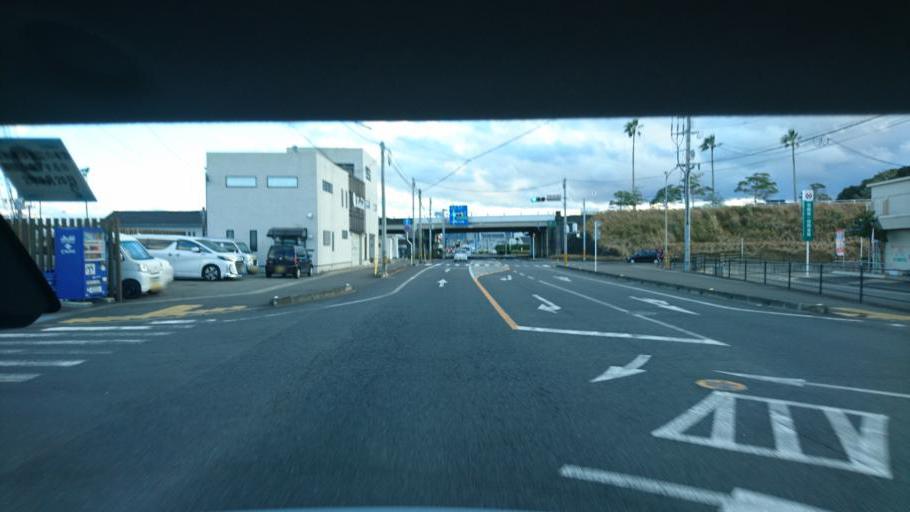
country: JP
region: Miyazaki
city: Miyazaki-shi
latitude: 31.8682
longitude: 131.4318
